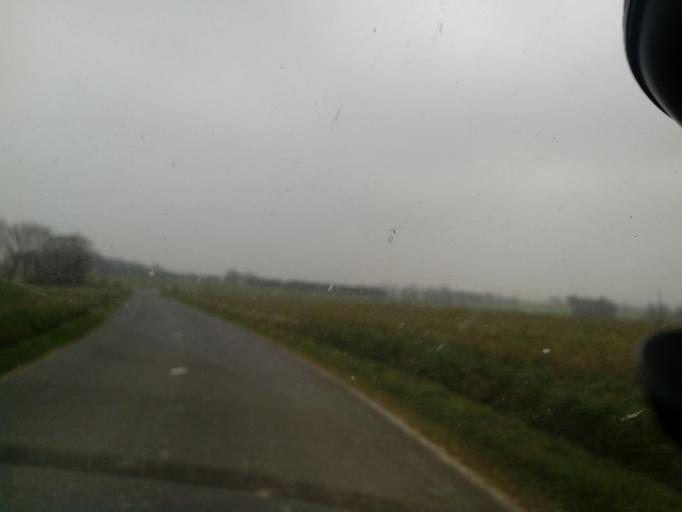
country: FR
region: Brittany
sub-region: Departement d'Ille-et-Vilaine
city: Gael
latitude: 48.1612
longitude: -2.2775
